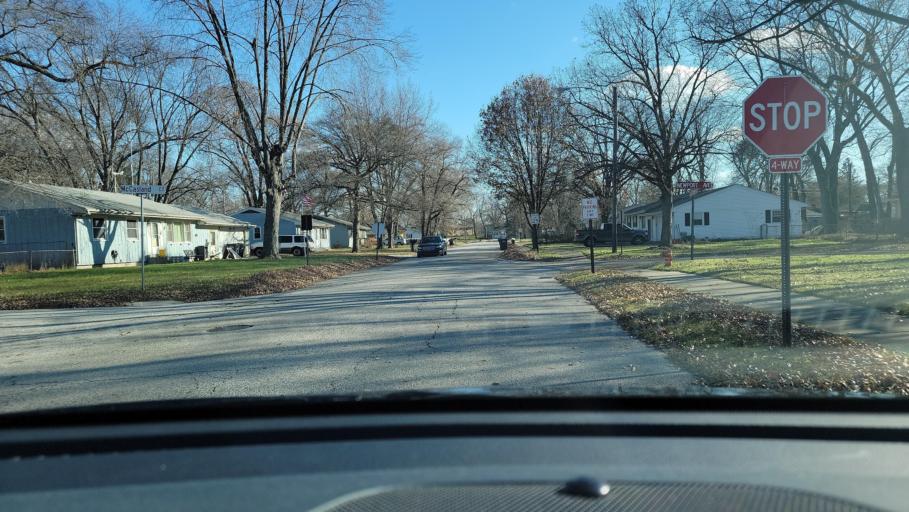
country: US
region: Indiana
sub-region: Porter County
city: Portage
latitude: 41.5830
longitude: -87.1904
